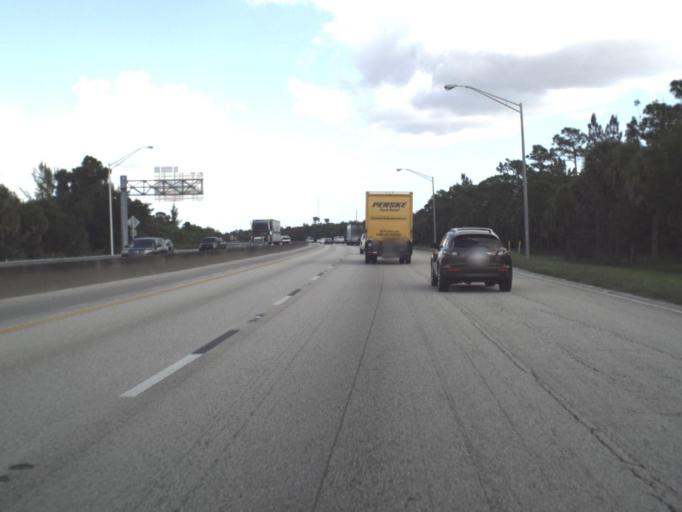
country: US
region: Florida
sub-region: Palm Beach County
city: Plantation Mobile Home Park
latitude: 26.7139
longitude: -80.1373
